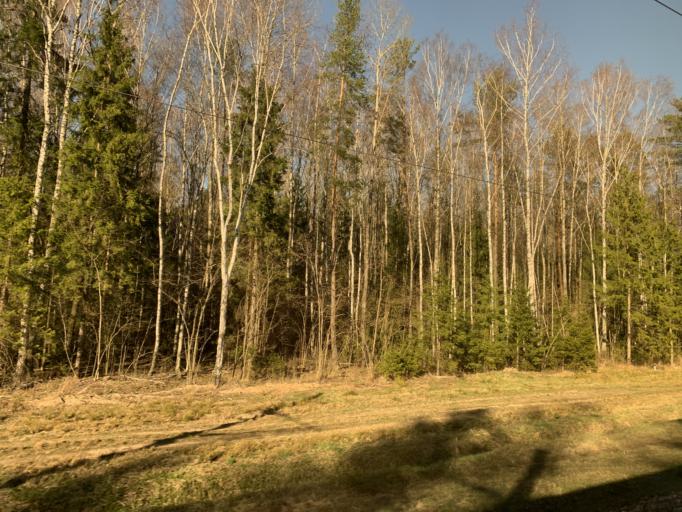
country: BY
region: Grodnenskaya
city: Smarhon'
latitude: 54.4865
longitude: 26.3147
